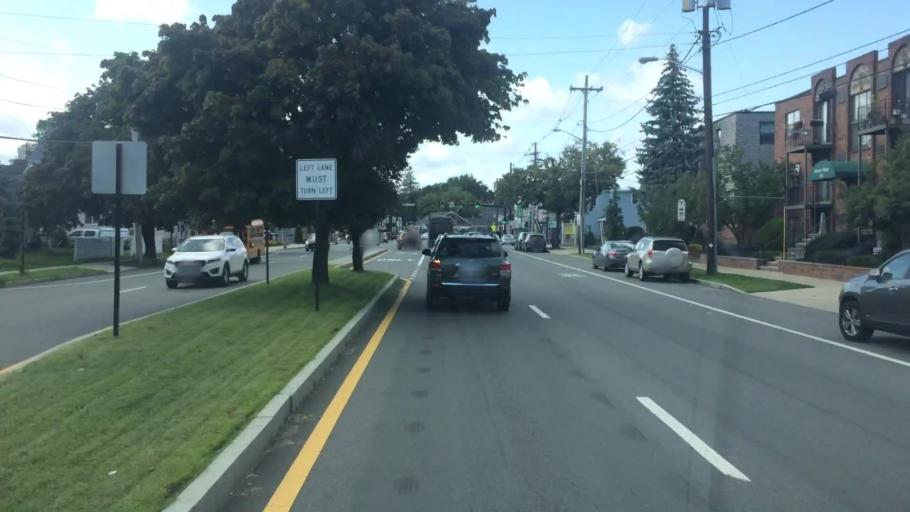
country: US
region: Massachusetts
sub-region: Essex County
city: Lynn
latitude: 42.4841
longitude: -70.9588
